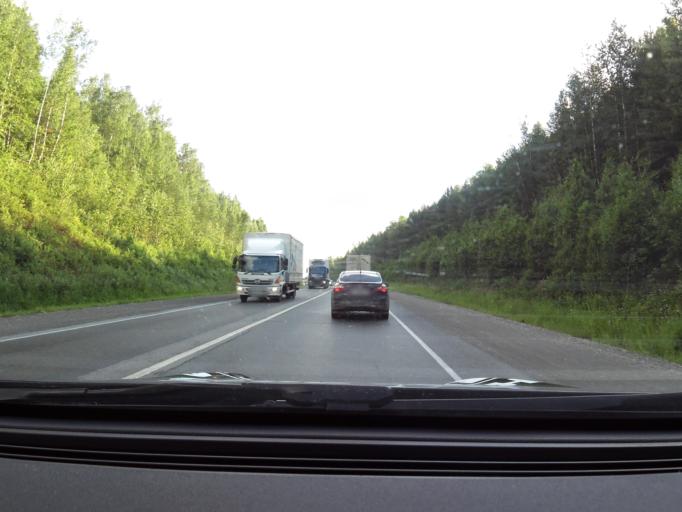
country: RU
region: Sverdlovsk
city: Talitsa
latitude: 56.8413
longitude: 60.0078
